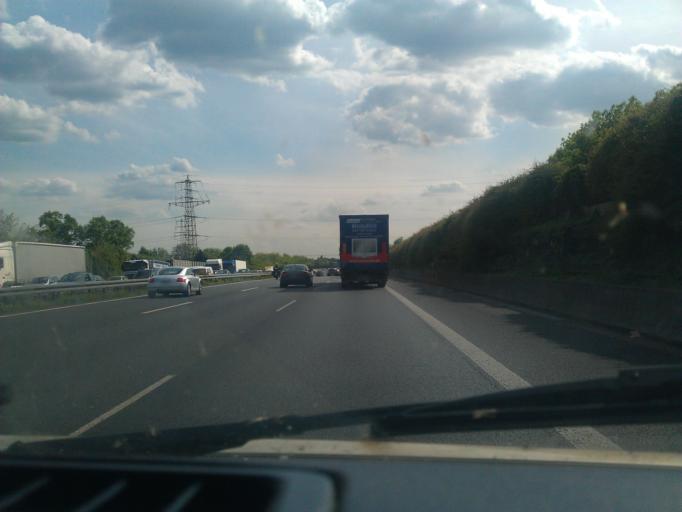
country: DE
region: North Rhine-Westphalia
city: Meiderich
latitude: 51.5019
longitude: 6.8218
